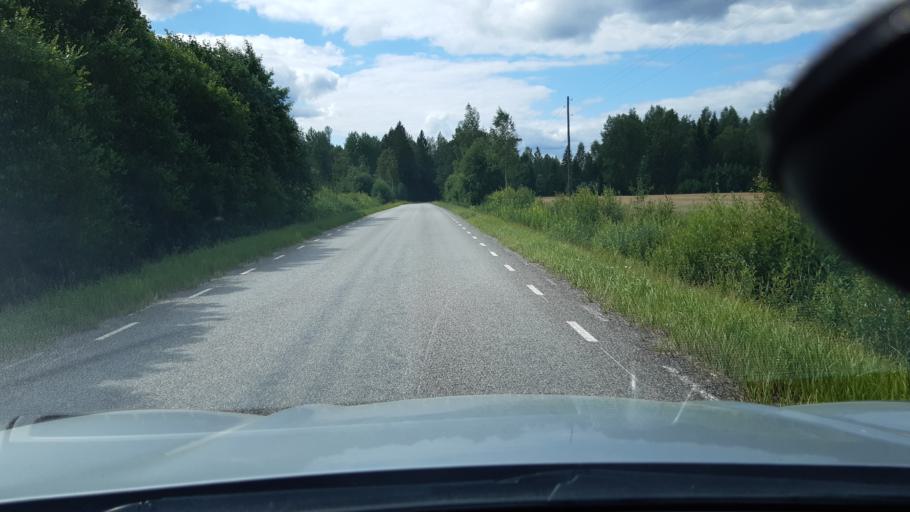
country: EE
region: Raplamaa
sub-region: Jaervakandi vald
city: Jarvakandi
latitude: 58.7951
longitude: 24.8622
